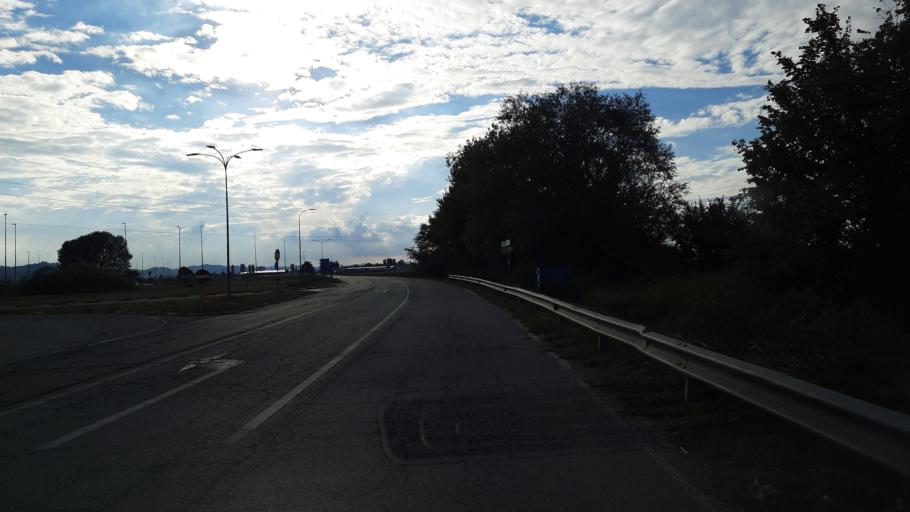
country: IT
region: Piedmont
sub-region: Provincia di Vercelli
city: Palazzolo Vercellese
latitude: 45.1909
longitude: 8.2527
